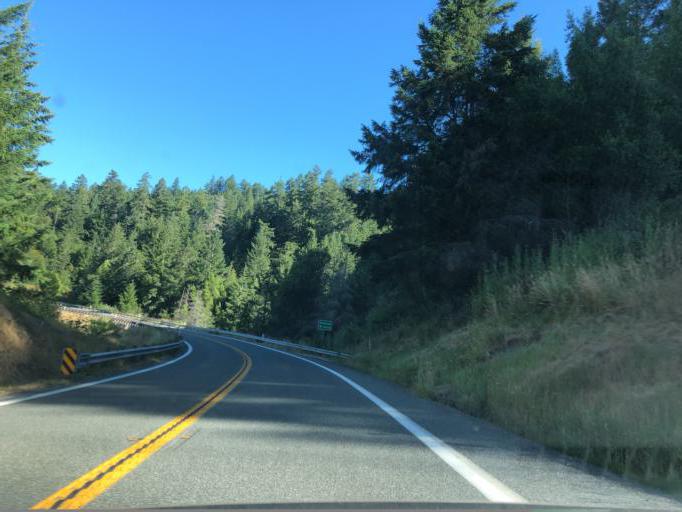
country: US
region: California
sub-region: Humboldt County
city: Willow Creek
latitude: 40.9214
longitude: -123.7947
